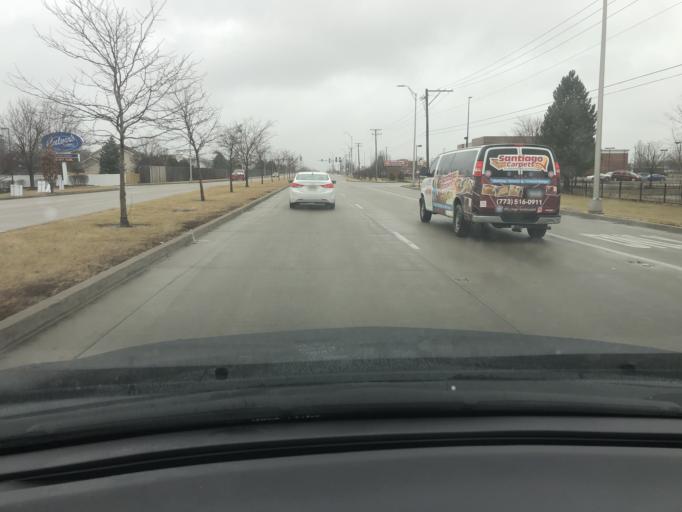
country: US
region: Illinois
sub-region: Will County
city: Shorewood
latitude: 41.5492
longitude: -88.1998
